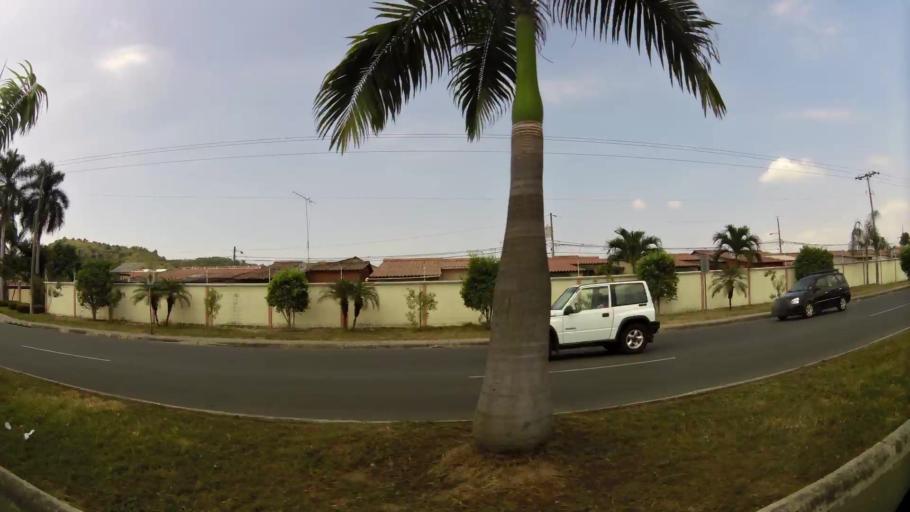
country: EC
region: Guayas
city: El Triunfo
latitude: -2.0440
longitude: -79.9153
